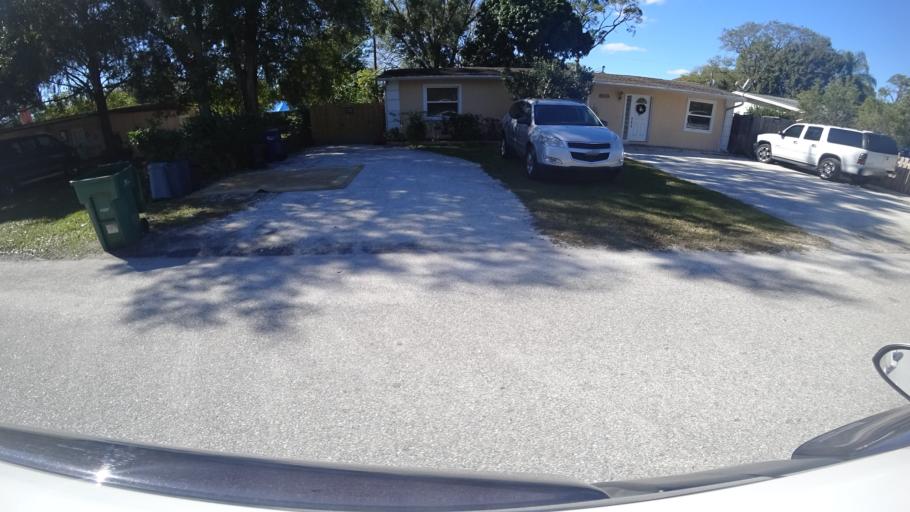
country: US
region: Florida
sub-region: Manatee County
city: Whitfield
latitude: 27.4333
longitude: -82.5534
